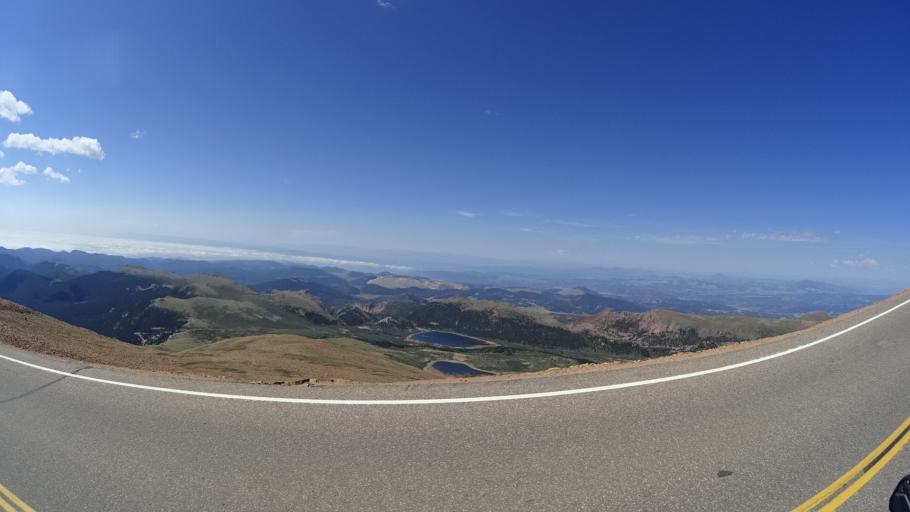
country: US
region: Colorado
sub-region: El Paso County
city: Cascade-Chipita Park
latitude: 38.8385
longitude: -105.0447
